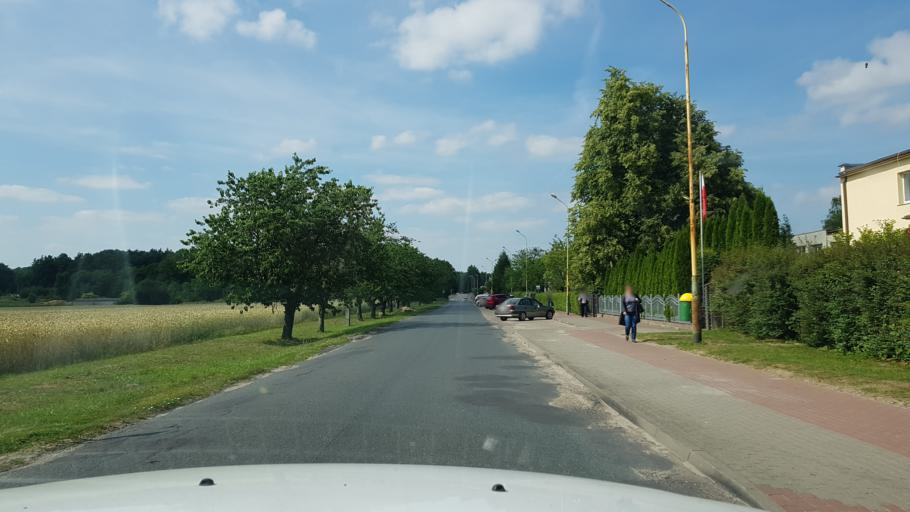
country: PL
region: West Pomeranian Voivodeship
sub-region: Powiat goleniowski
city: Osina
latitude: 53.6060
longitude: 15.0119
